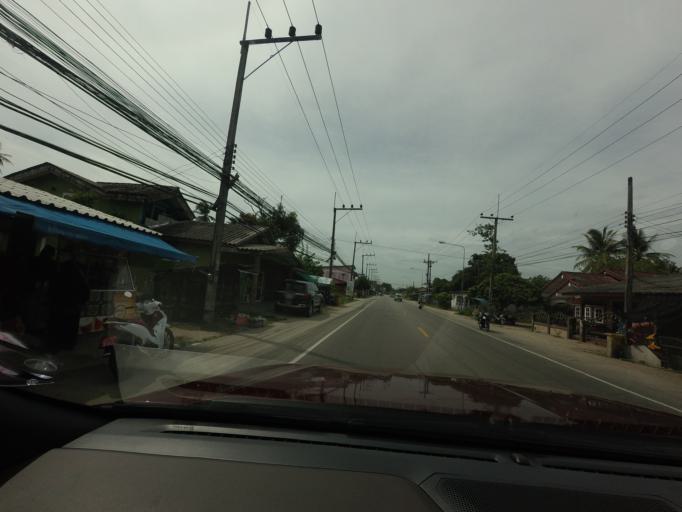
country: TH
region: Narathiwat
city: Tak Bai
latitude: 6.2525
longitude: 102.0637
